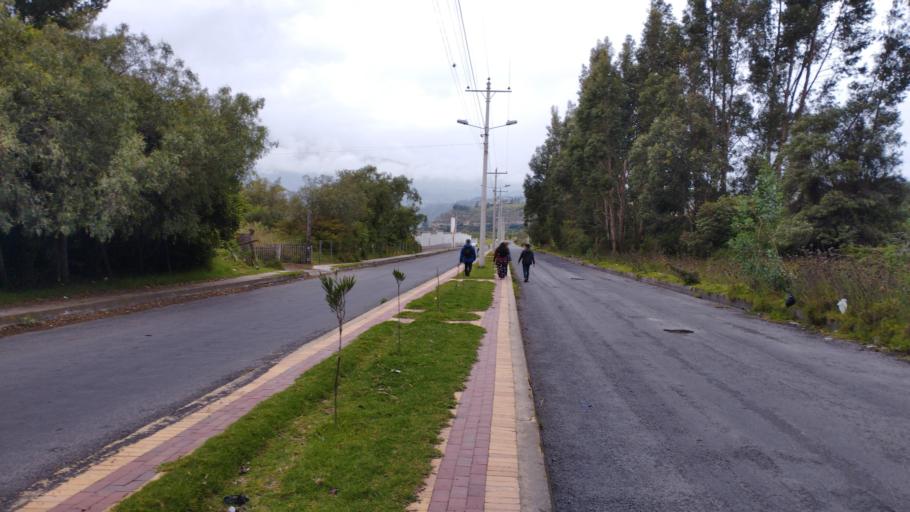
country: EC
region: Chimborazo
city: Guano
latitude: -1.6112
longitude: -78.6088
